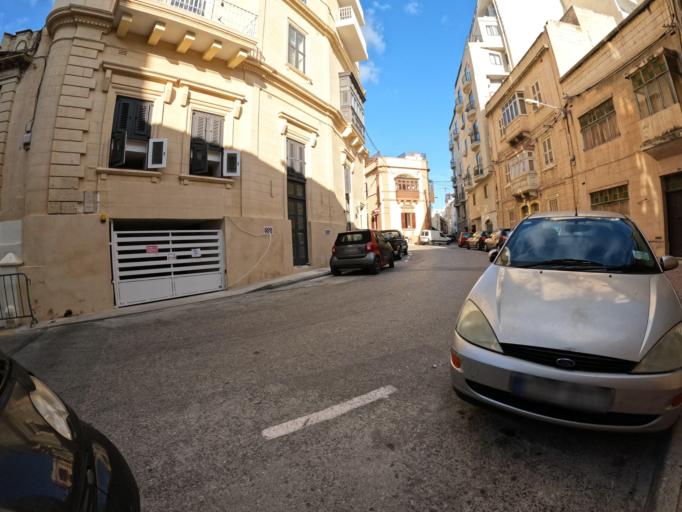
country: MT
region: Saint Julian
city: San Giljan
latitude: 35.9163
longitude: 14.4931
